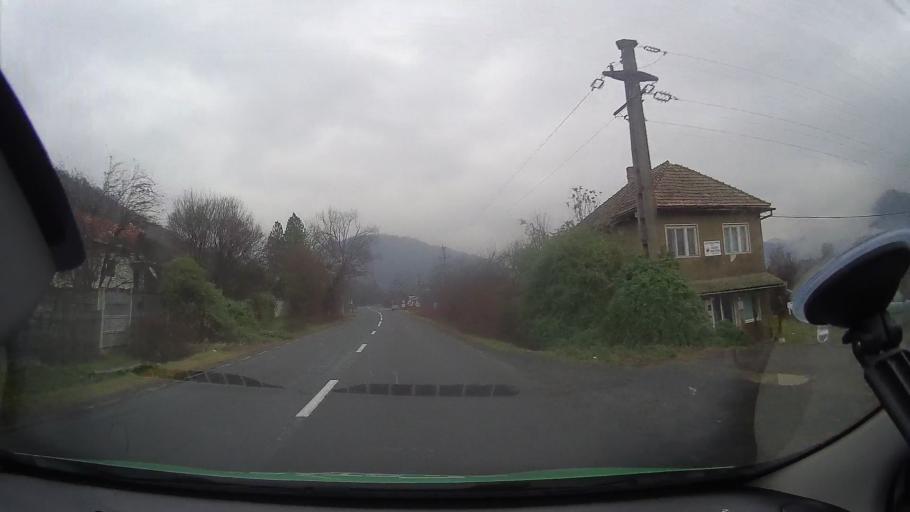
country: RO
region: Arad
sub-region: Comuna Plescuta
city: Plescuta
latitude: 46.2954
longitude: 22.4348
